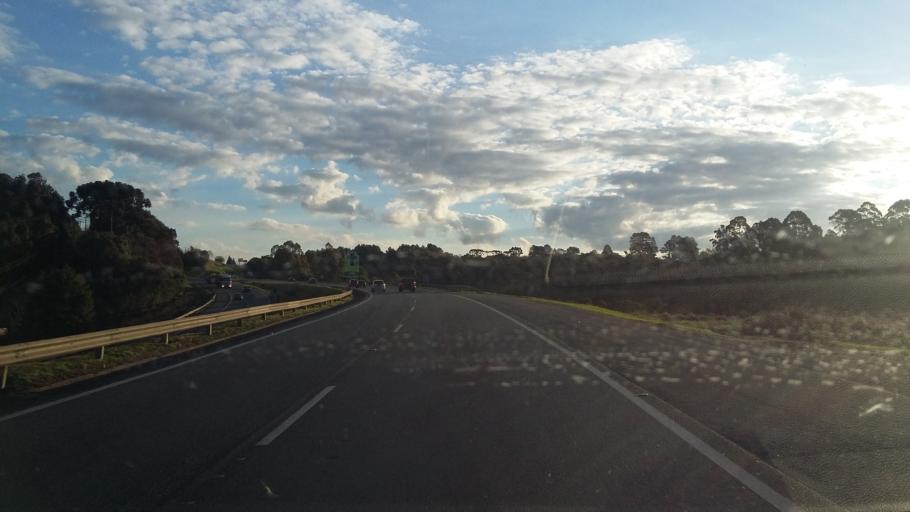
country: BR
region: Parana
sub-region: Campo Largo
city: Campo Largo
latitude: -25.4434
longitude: -49.4648
